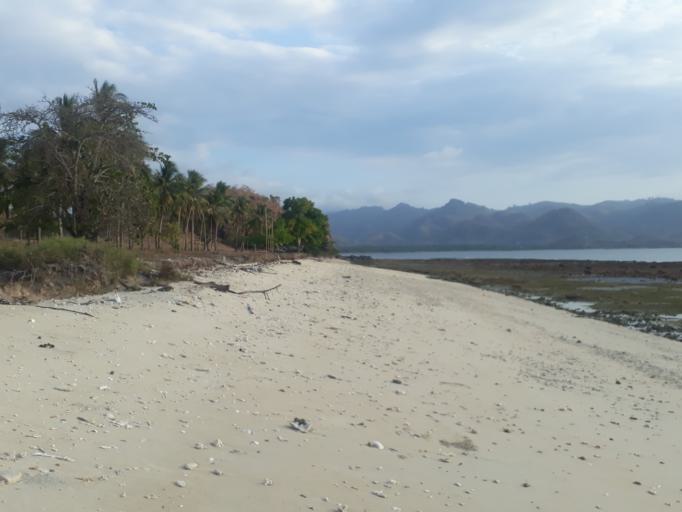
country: ID
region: West Nusa Tenggara
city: Tawun
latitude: -8.7343
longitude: 115.8829
